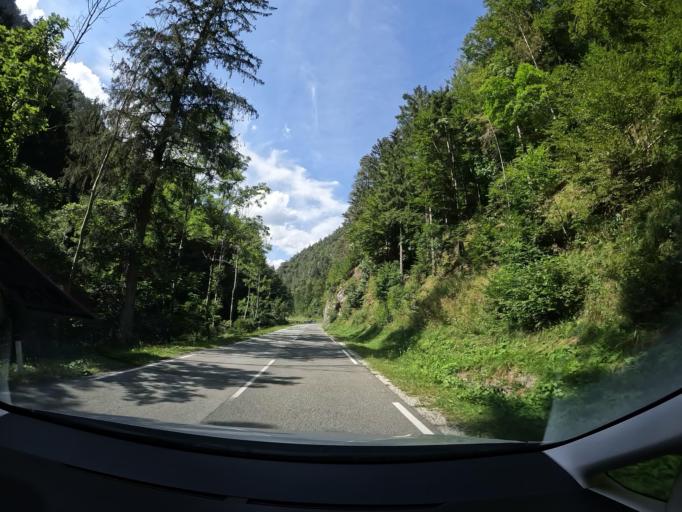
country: SI
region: Jezersko
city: Zgornje Jezersko
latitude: 46.3534
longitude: 14.4712
